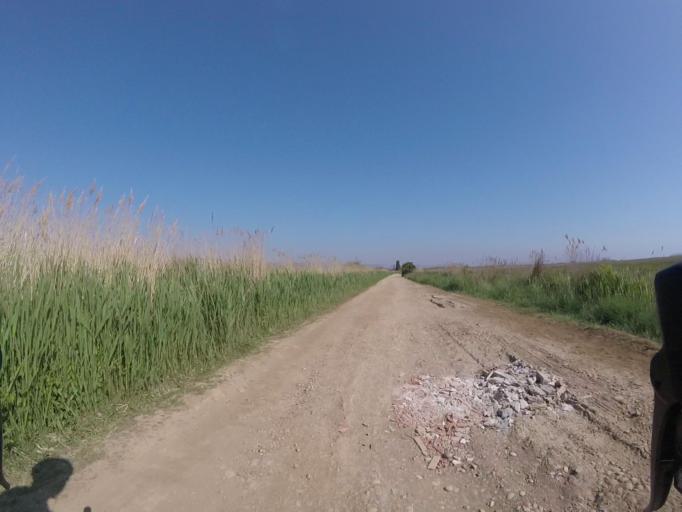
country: ES
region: Valencia
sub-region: Provincia de Castello
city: Orpesa/Oropesa del Mar
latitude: 40.1411
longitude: 0.1639
